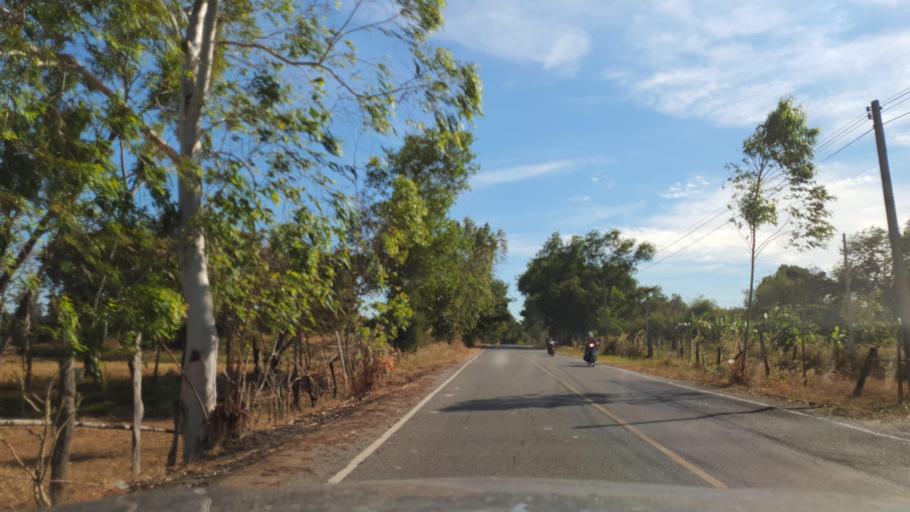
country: TH
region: Kalasin
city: Khao Wong
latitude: 16.6190
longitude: 104.1357
